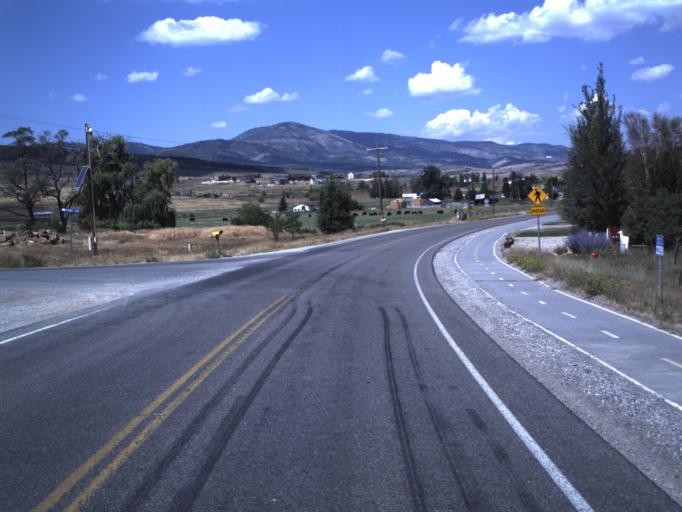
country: US
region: Idaho
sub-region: Bear Lake County
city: Paris
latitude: 41.9100
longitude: -111.3899
